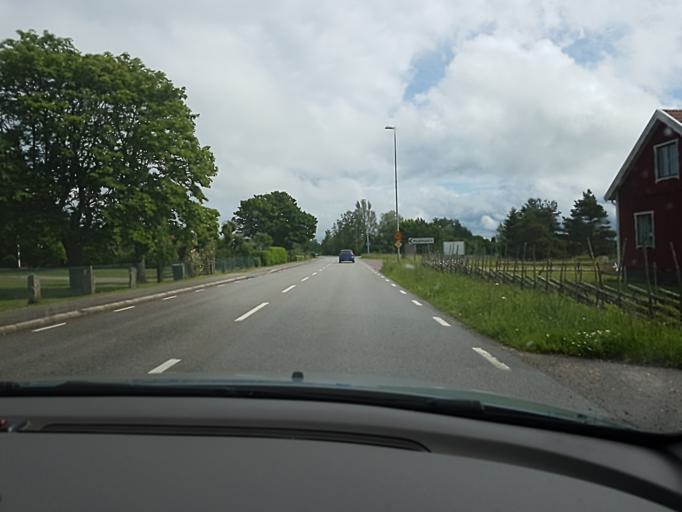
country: SE
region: Uppsala
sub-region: Osthammars Kommun
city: OEsthammar
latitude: 60.2868
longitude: 18.2877
